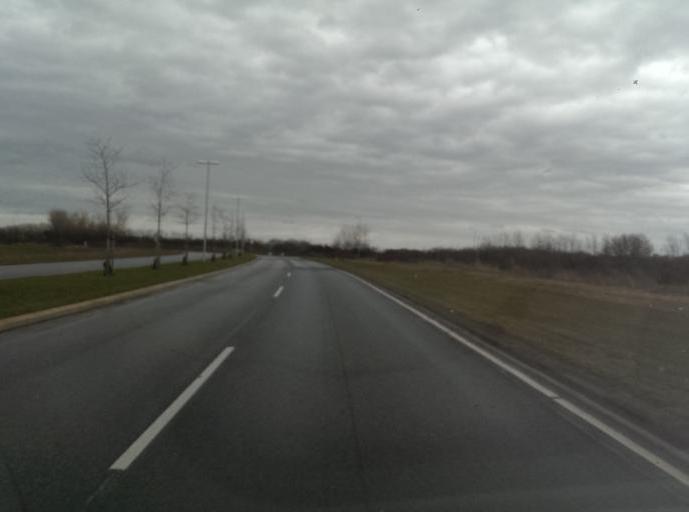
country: DK
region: South Denmark
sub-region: Esbjerg Kommune
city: Esbjerg
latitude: 55.5110
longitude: 8.5012
